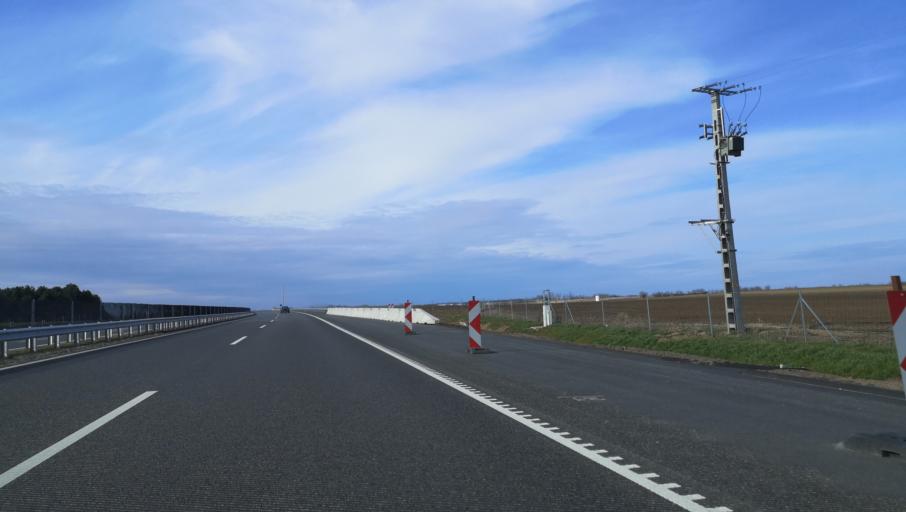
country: HU
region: Pest
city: Monor
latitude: 47.3733
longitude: 19.4741
